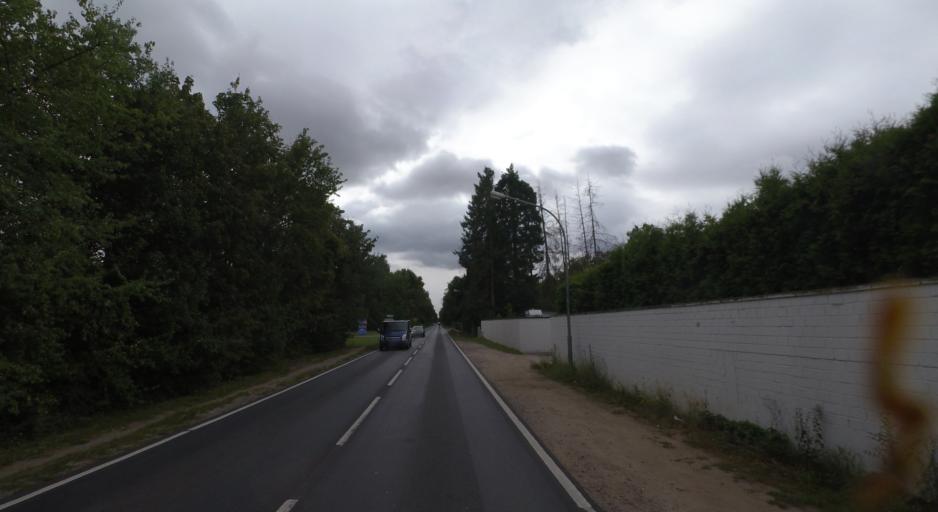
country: DE
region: Hesse
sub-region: Regierungsbezirk Darmstadt
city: Seligenstadt
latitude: 50.0337
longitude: 8.9845
